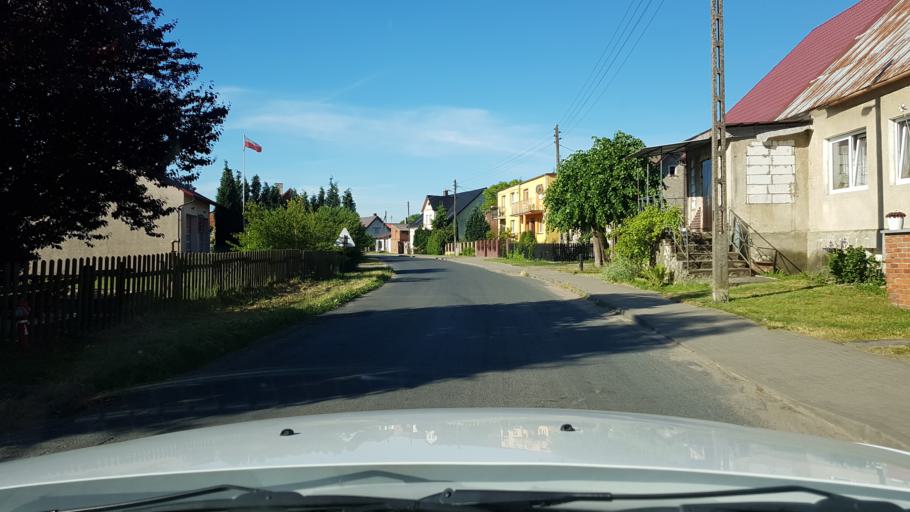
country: PL
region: West Pomeranian Voivodeship
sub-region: Powiat pyrzycki
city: Bielice
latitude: 53.2223
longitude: 14.6108
